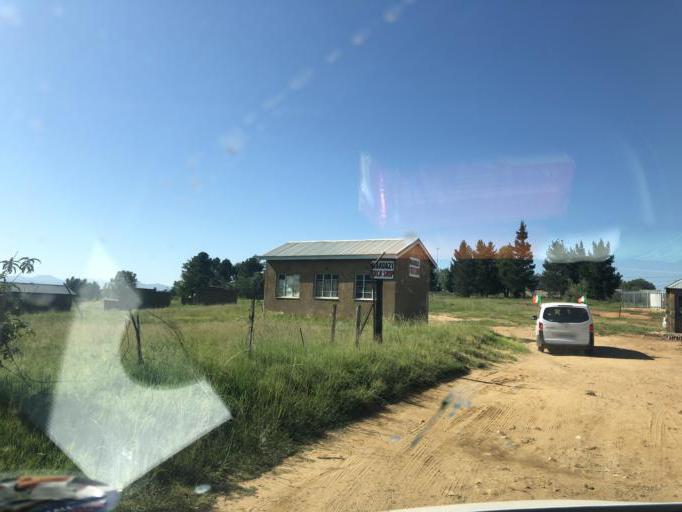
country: LS
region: Maseru
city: Maseru
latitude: -29.3485
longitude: 27.5358
